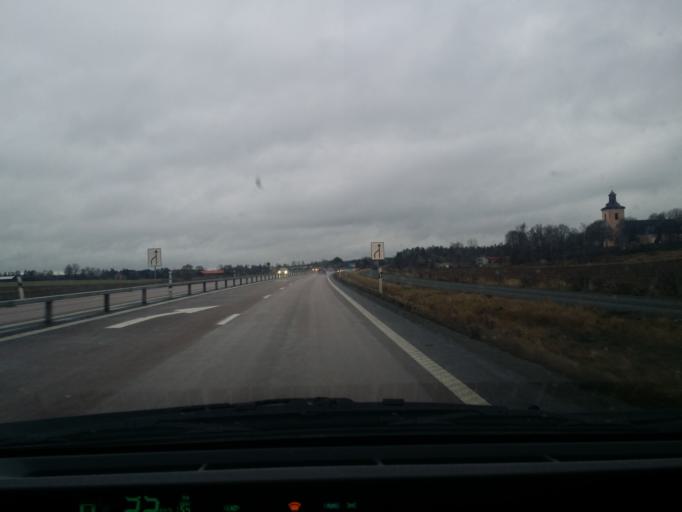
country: SE
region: Vaestmanland
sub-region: Sala Kommun
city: Sala
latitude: 59.8672
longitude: 16.5413
